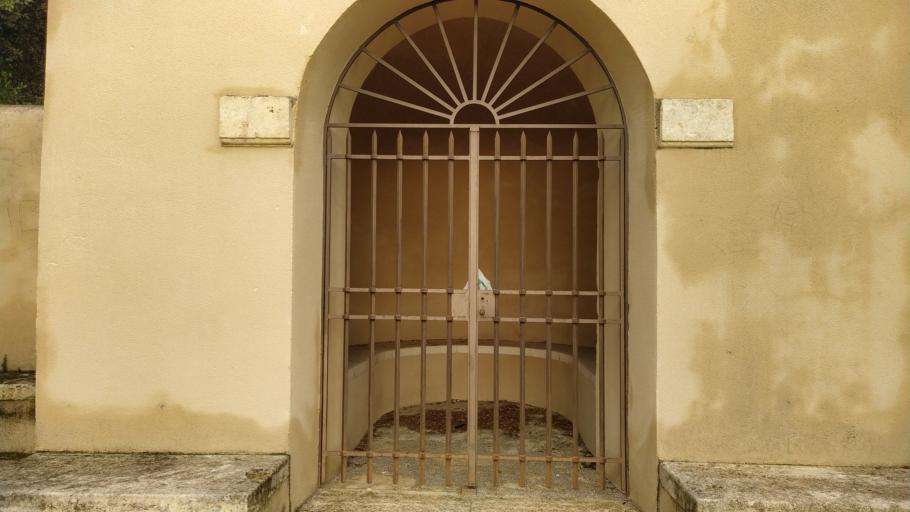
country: FR
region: Languedoc-Roussillon
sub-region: Departement du Gard
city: Poulx
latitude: 43.8712
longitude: 4.4041
